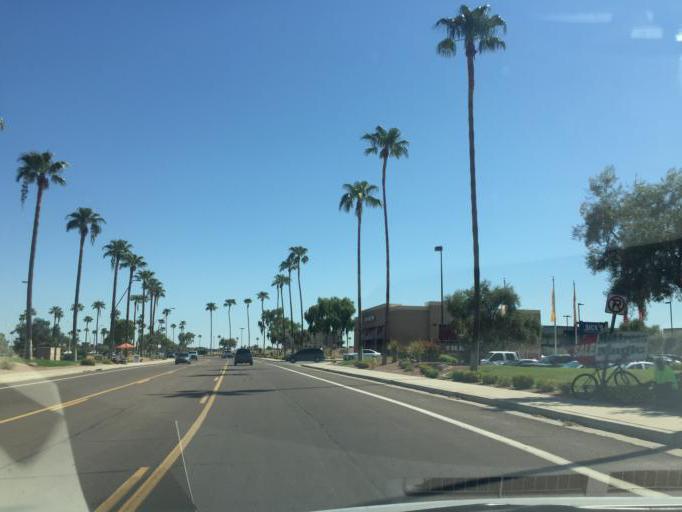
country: US
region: Arizona
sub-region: Maricopa County
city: Guadalupe
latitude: 33.3392
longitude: -111.9694
